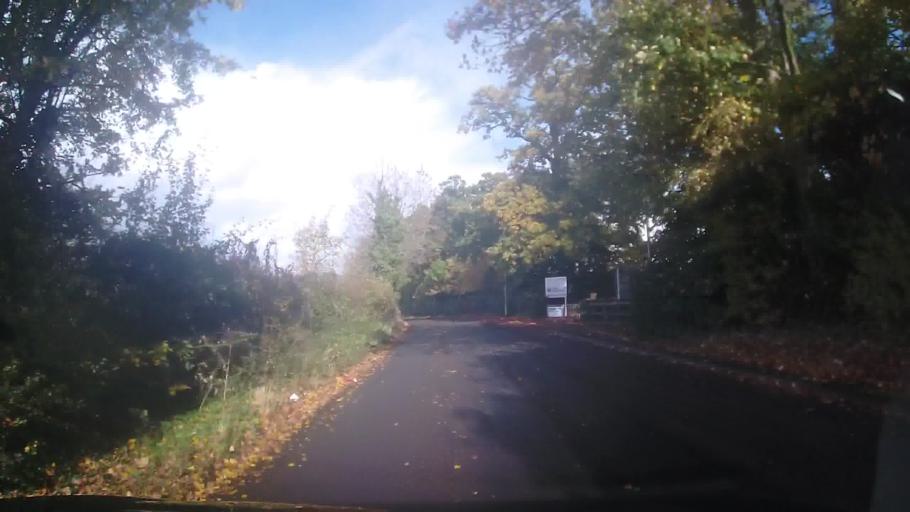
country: GB
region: England
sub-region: Shropshire
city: Whitchurch
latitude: 52.9575
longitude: -2.6799
